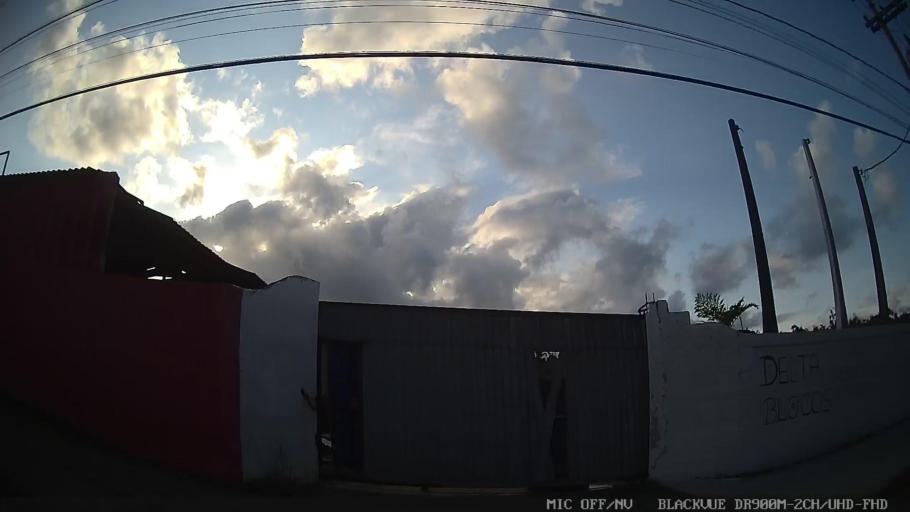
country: BR
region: Sao Paulo
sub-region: Itanhaem
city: Itanhaem
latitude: -24.1676
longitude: -46.8403
